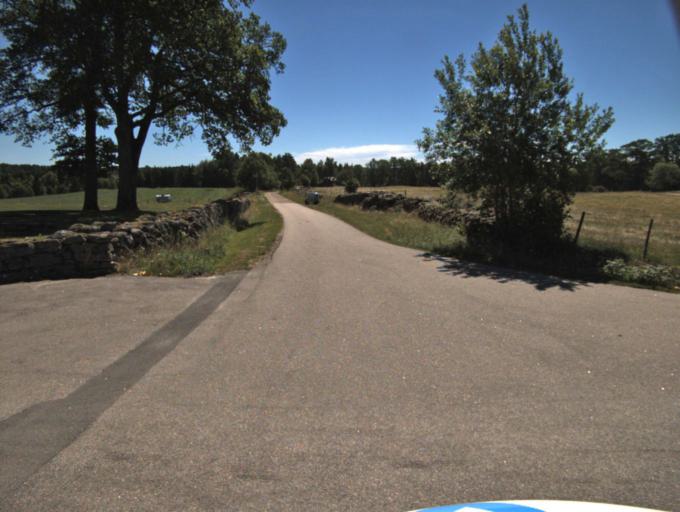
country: SE
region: Vaestra Goetaland
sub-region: Ulricehamns Kommun
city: Ulricehamn
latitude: 57.6596
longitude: 13.4323
